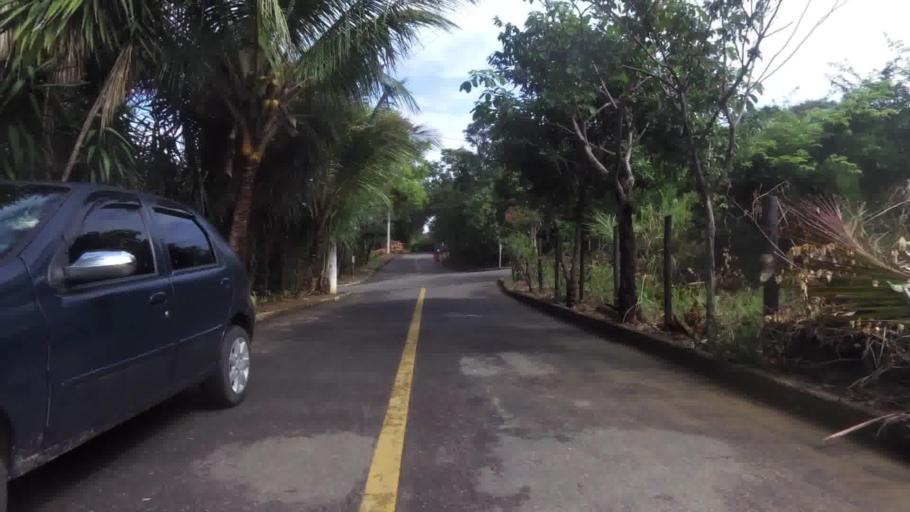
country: BR
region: Espirito Santo
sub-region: Piuma
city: Piuma
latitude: -20.8308
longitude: -40.7022
